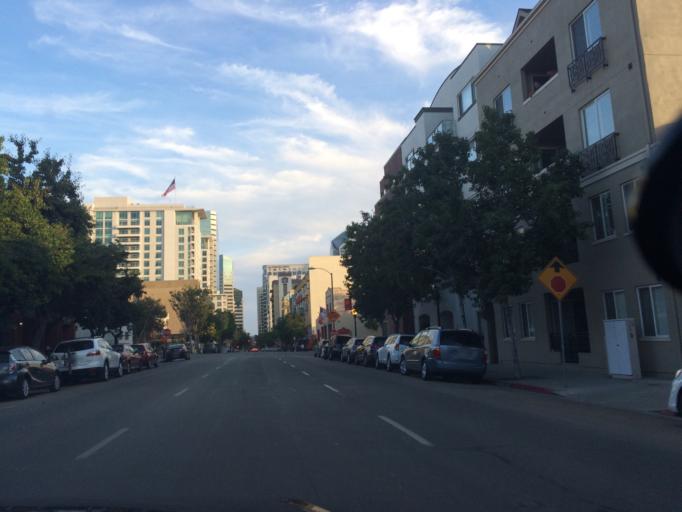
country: US
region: California
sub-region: San Diego County
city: San Diego
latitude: 32.7226
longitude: -117.1674
